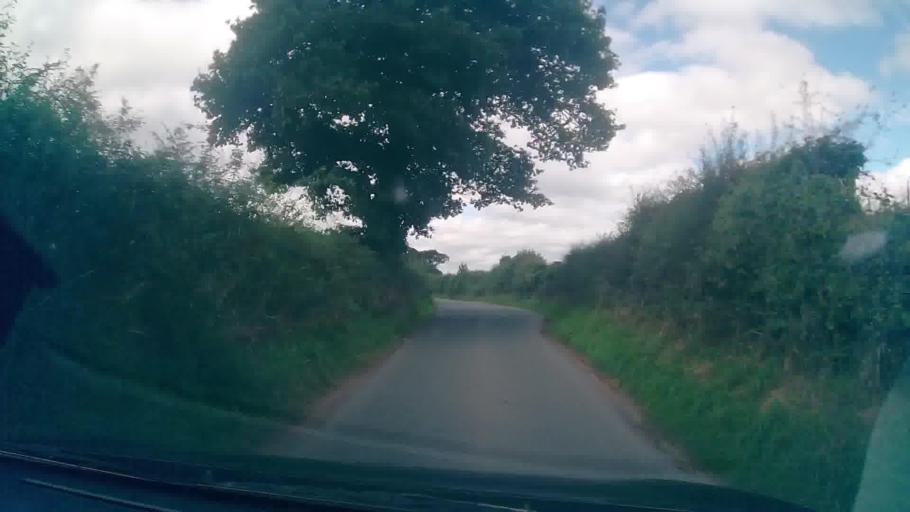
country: GB
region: England
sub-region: Shropshire
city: Whitchurch
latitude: 52.9407
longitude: -2.7316
